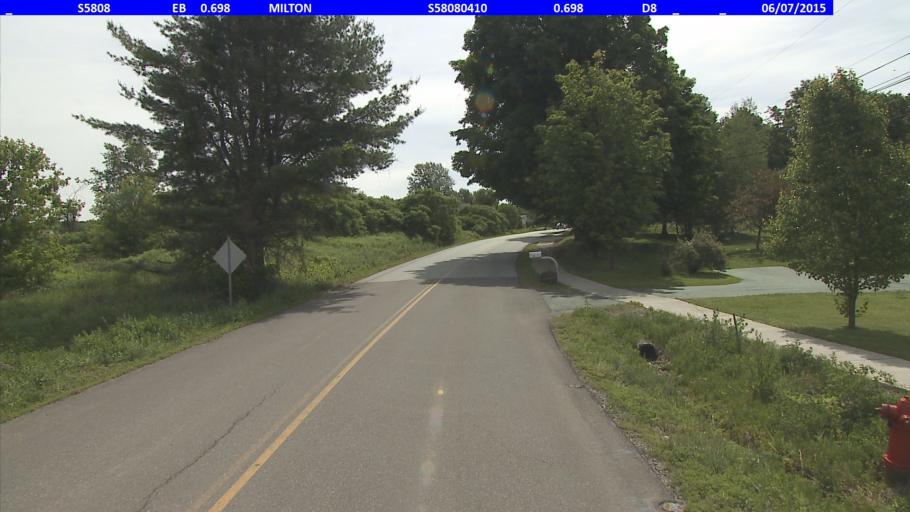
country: US
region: Vermont
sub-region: Chittenden County
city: Milton
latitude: 44.6387
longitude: -73.0997
